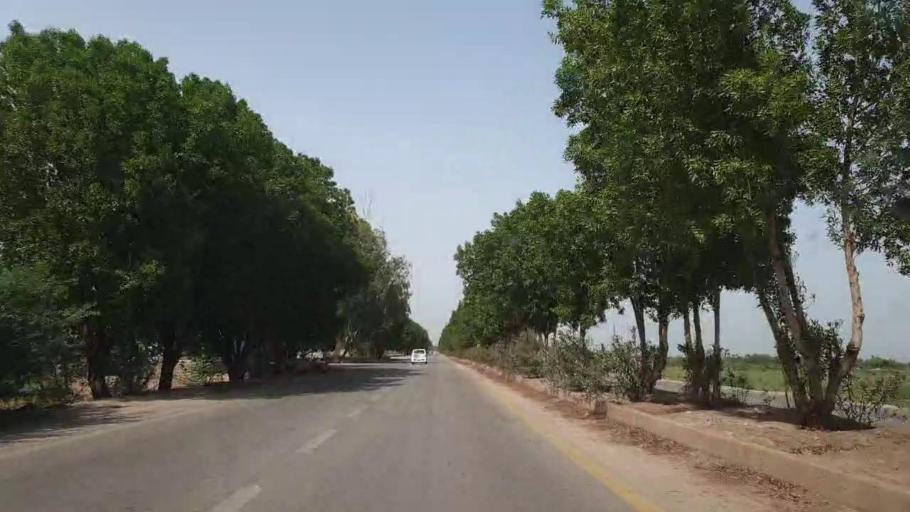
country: PK
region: Sindh
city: Sakrand
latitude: 26.1654
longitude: 68.2802
